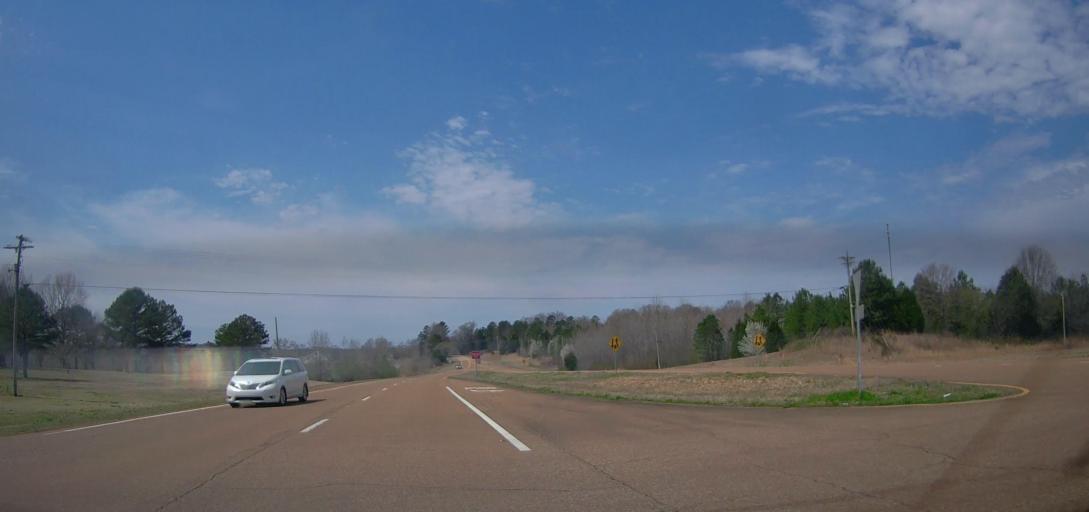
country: US
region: Mississippi
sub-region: Benton County
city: Ashland
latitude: 34.6184
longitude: -89.2068
